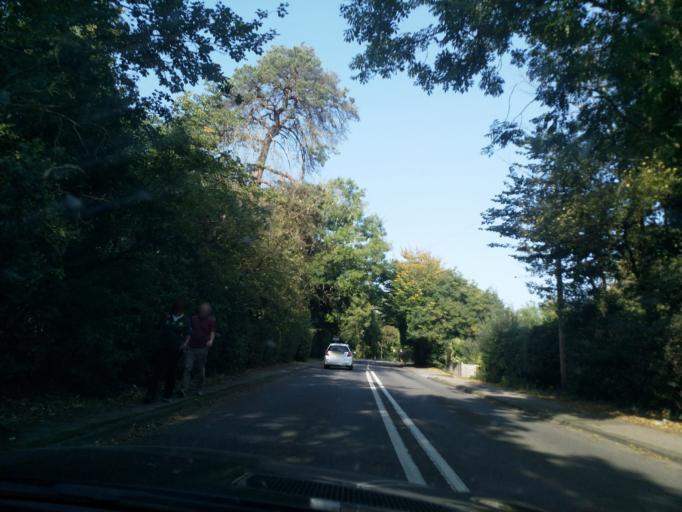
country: GB
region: England
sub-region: Solihull
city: Knowle
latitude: 52.3838
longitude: -1.7346
